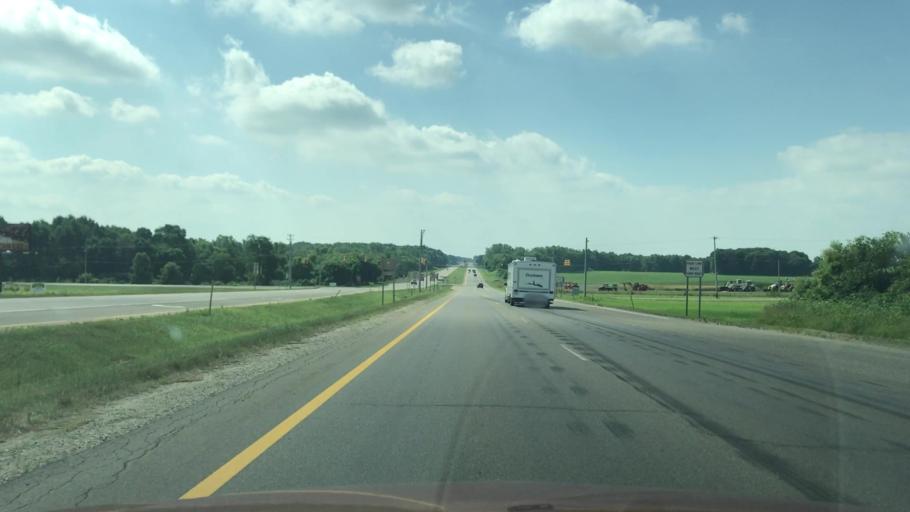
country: US
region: Michigan
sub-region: Kent County
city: Sparta
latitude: 43.1183
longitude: -85.7066
